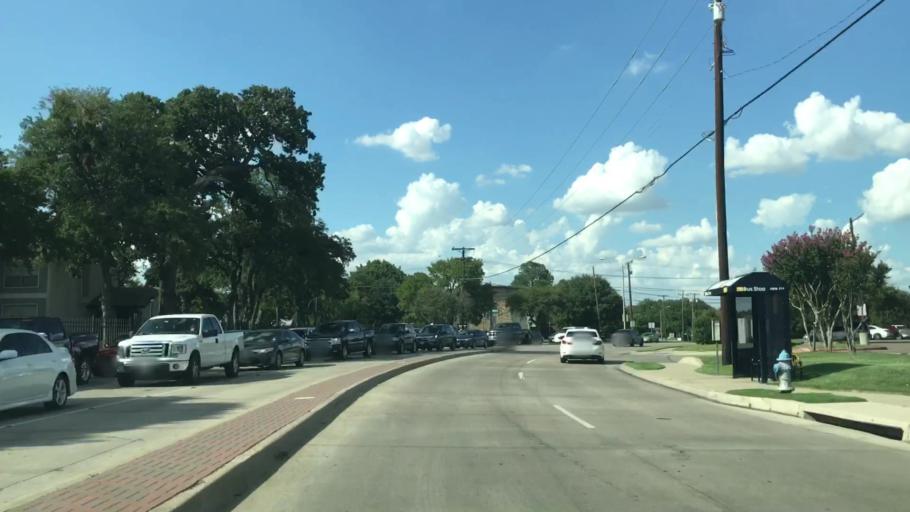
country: US
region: Texas
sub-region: Dallas County
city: Irving
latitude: 32.8445
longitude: -96.9513
